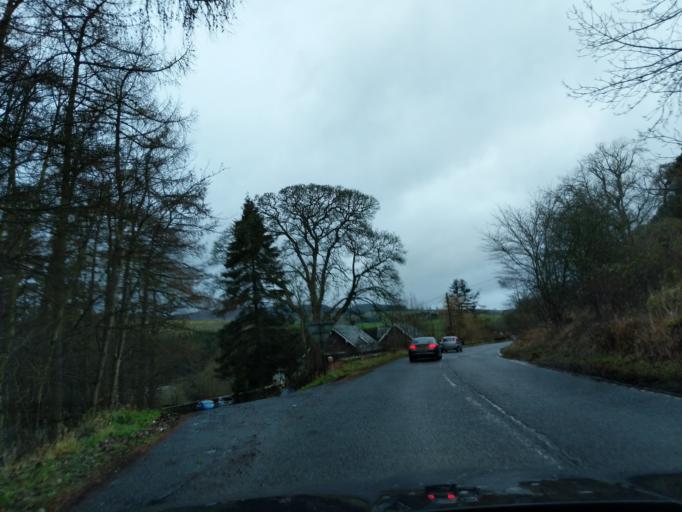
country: GB
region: Scotland
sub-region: The Scottish Borders
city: Galashiels
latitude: 55.6523
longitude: -2.8645
